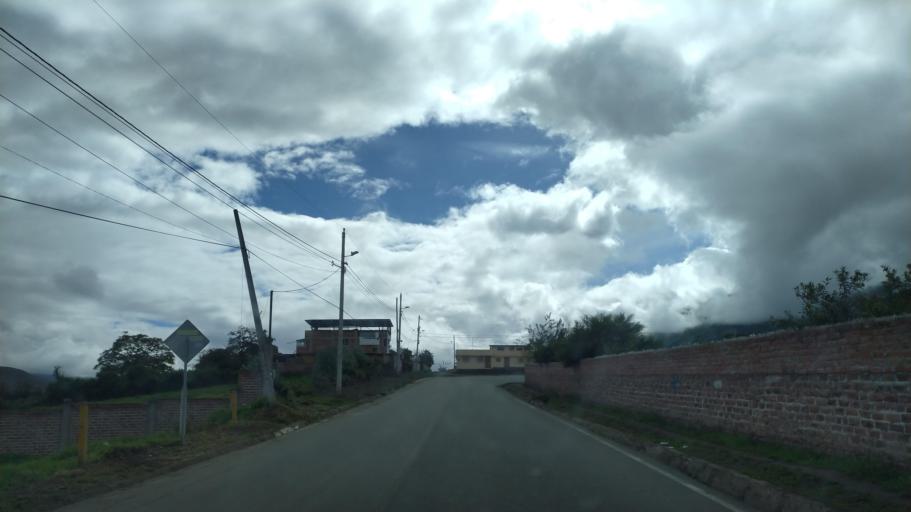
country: EC
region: Chimborazo
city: Riobamba
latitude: -1.6581
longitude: -78.5731
